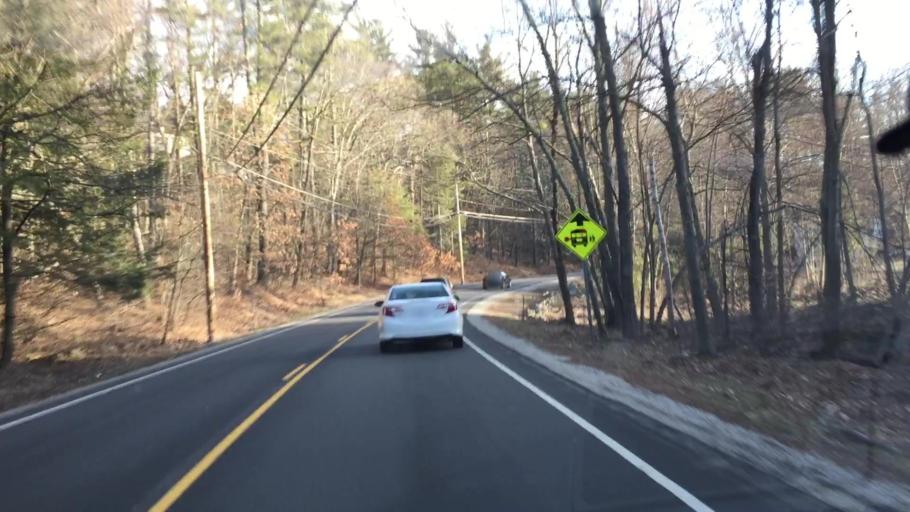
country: US
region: New Hampshire
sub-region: Rockingham County
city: Londonderry
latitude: 42.8309
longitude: -71.3651
